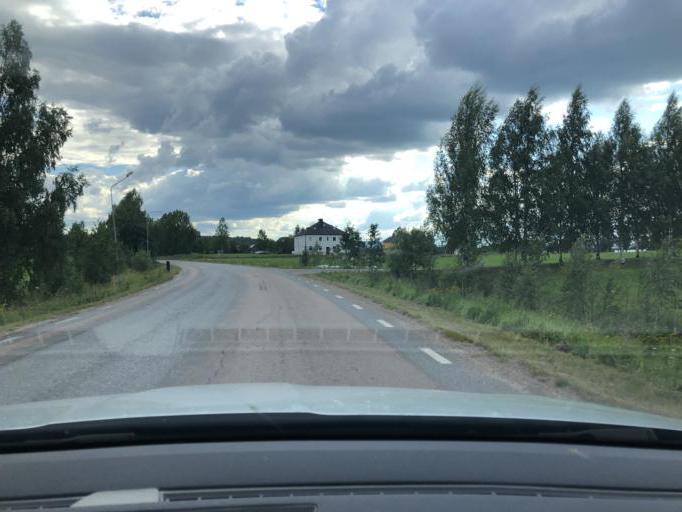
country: SE
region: Vaesternorrland
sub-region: Solleftea Kommun
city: Solleftea
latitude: 63.1883
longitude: 17.0689
